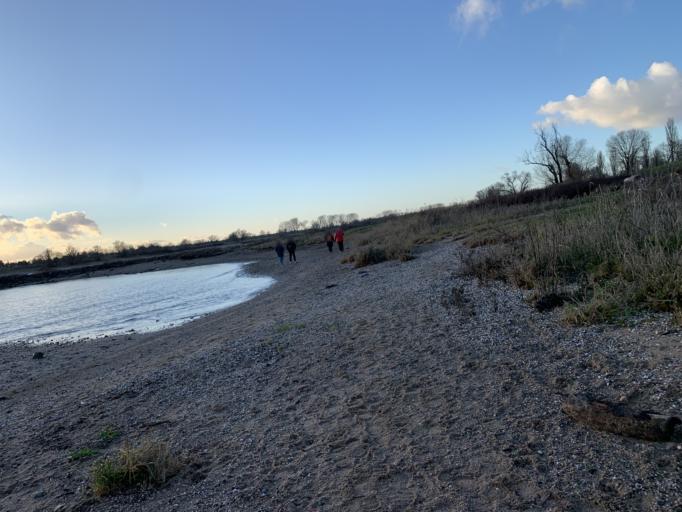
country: DE
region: North Rhine-Westphalia
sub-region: Regierungsbezirk Dusseldorf
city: Meerbusch
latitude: 51.2595
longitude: 6.7240
